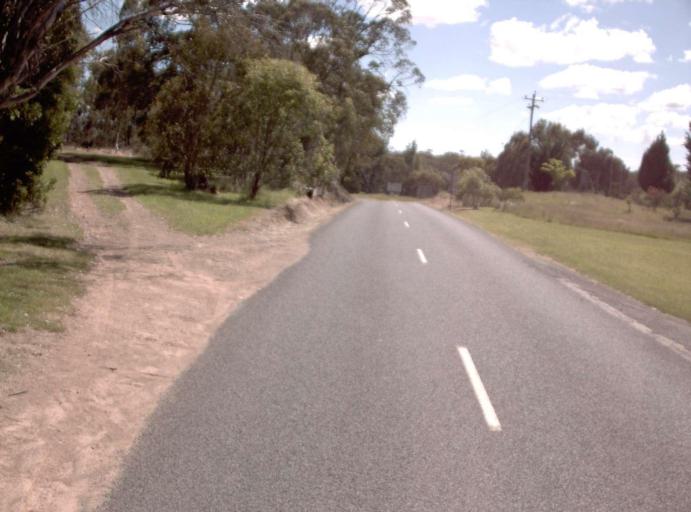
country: AU
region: New South Wales
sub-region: Bombala
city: Bombala
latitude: -37.0490
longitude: 148.8109
